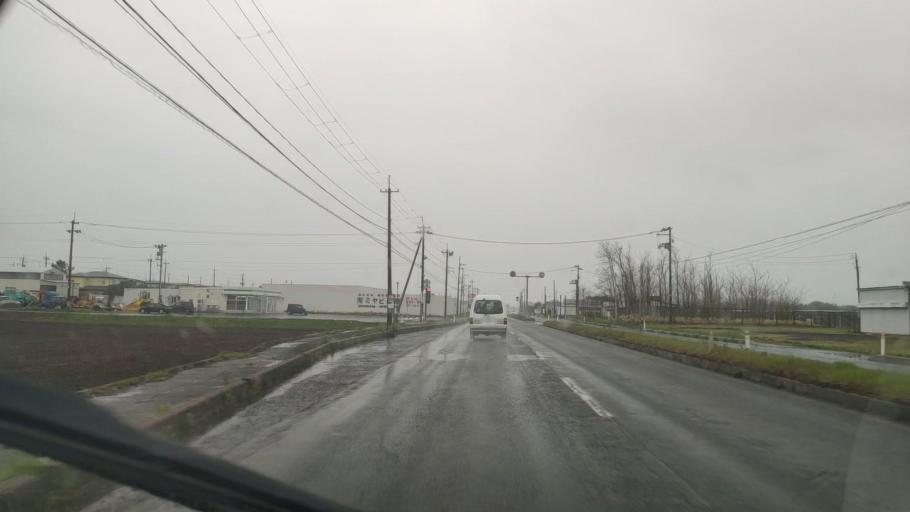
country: JP
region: Akita
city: Tenno
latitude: 39.8737
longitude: 139.9946
